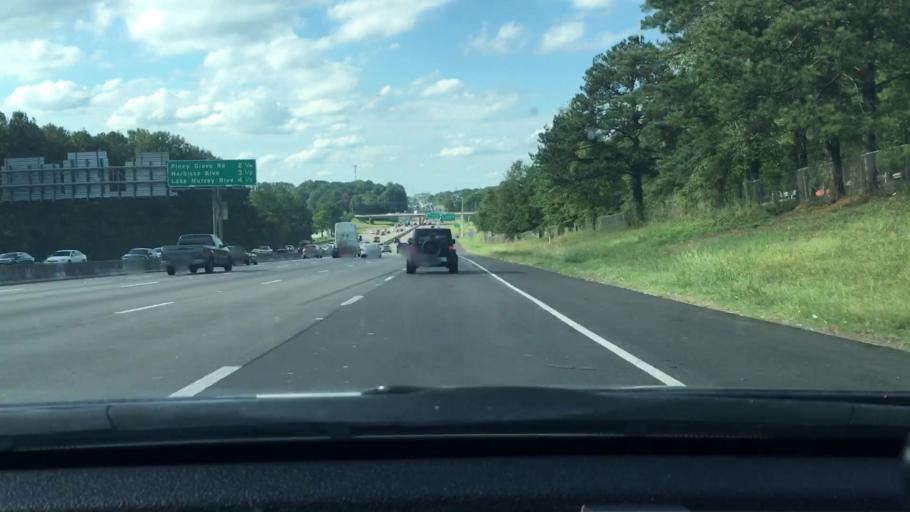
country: US
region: South Carolina
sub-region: Lexington County
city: Saint Andrews
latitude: 34.0399
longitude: -81.1133
